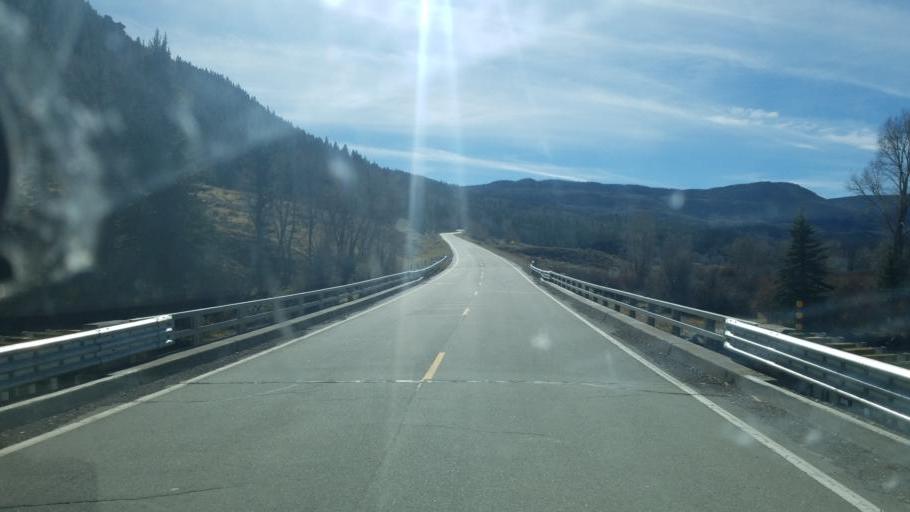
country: US
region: New Mexico
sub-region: Rio Arriba County
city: Chama
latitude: 37.1284
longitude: -106.3570
